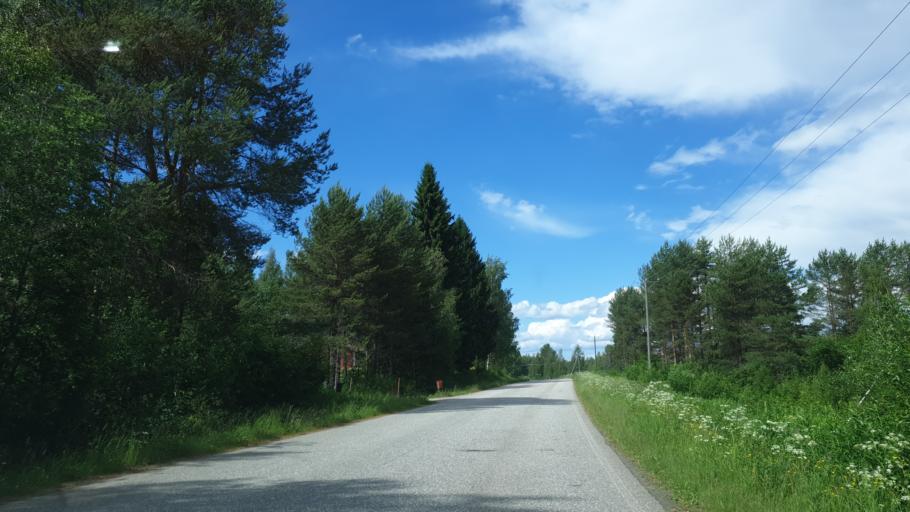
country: FI
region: Northern Savo
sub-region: Koillis-Savo
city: Kaavi
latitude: 62.9969
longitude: 28.7172
